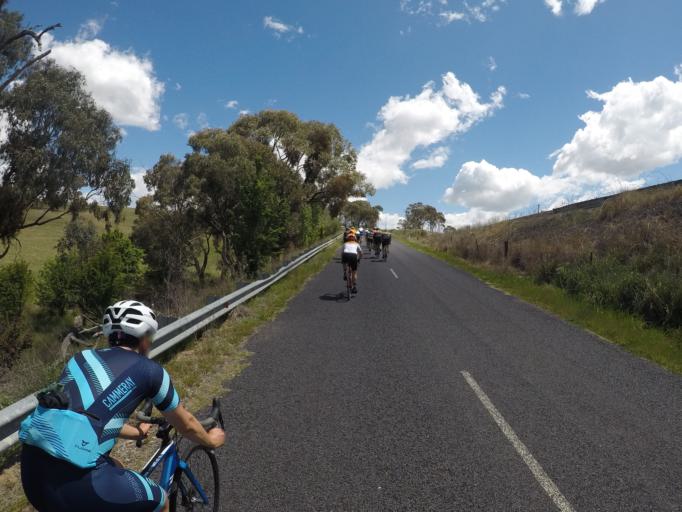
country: AU
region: New South Wales
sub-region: Blayney
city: Blayney
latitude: -33.5796
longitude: 149.4011
